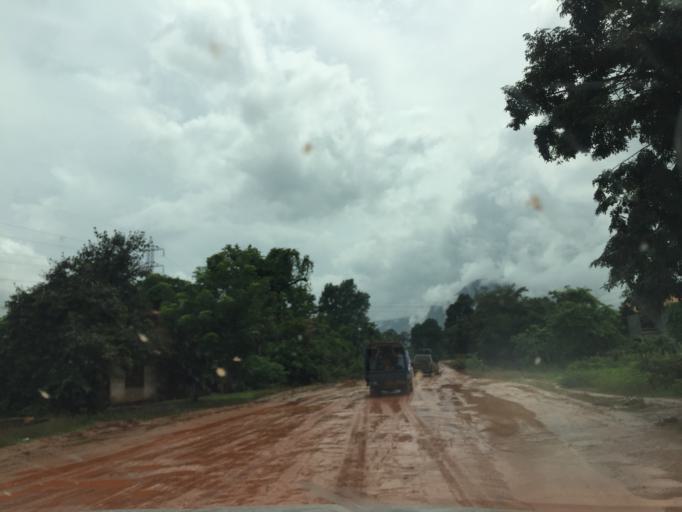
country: LA
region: Attapu
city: Attapu
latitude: 14.8088
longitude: 106.7749
